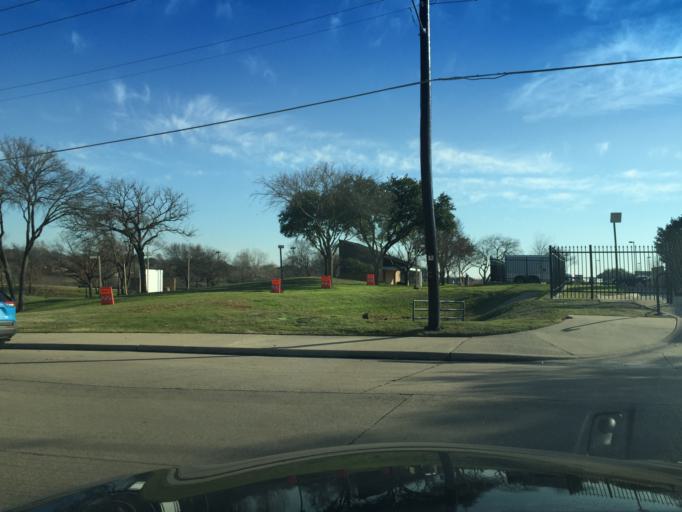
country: US
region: Texas
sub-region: Dallas County
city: Carrollton
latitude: 32.9771
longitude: -96.8858
